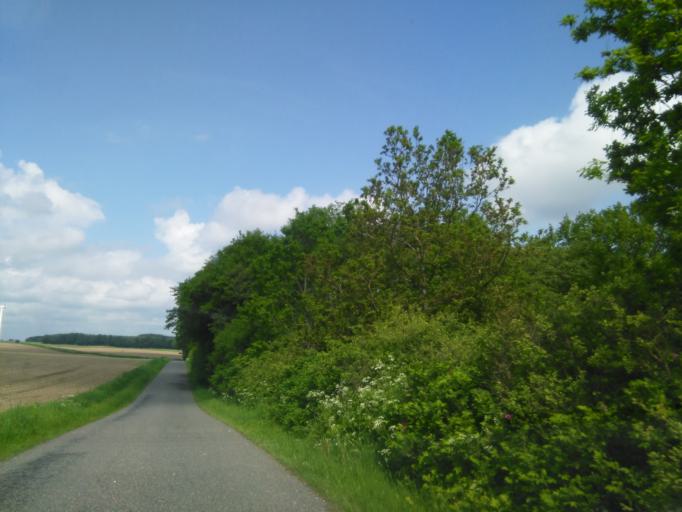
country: DK
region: Central Jutland
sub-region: Skanderborg Kommune
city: Galten
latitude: 56.2107
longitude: 9.9386
